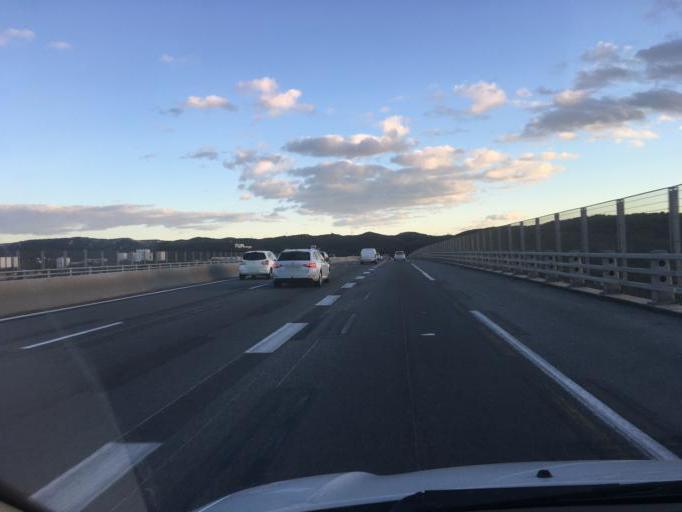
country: FR
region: Provence-Alpes-Cote d'Azur
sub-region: Departement des Bouches-du-Rhone
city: Martigues
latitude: 43.4026
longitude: 5.0420
